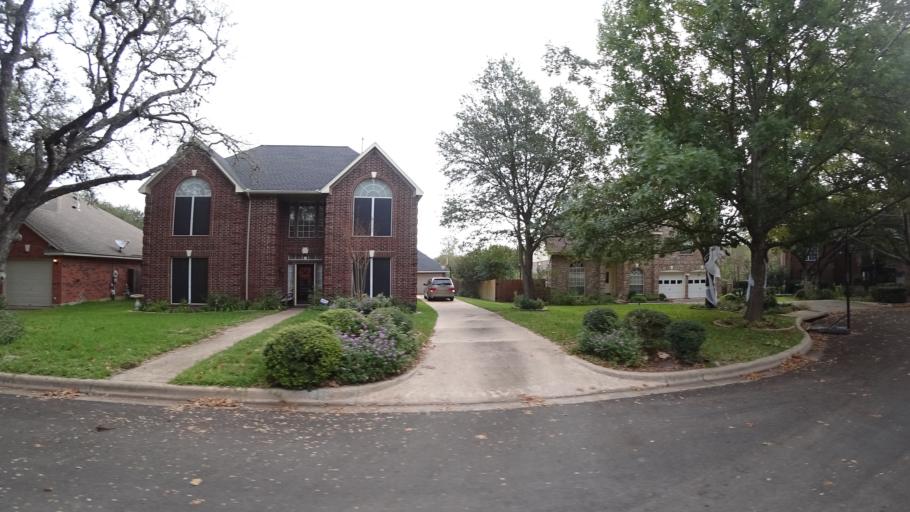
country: US
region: Texas
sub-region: Travis County
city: Shady Hollow
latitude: 30.1884
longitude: -97.8870
